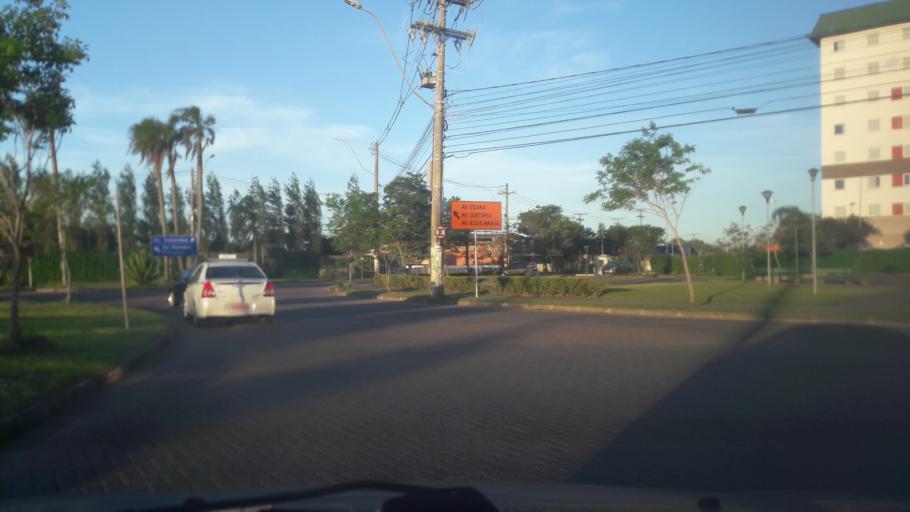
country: BR
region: Rio Grande do Sul
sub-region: Canoas
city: Canoas
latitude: -29.9880
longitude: -51.1712
